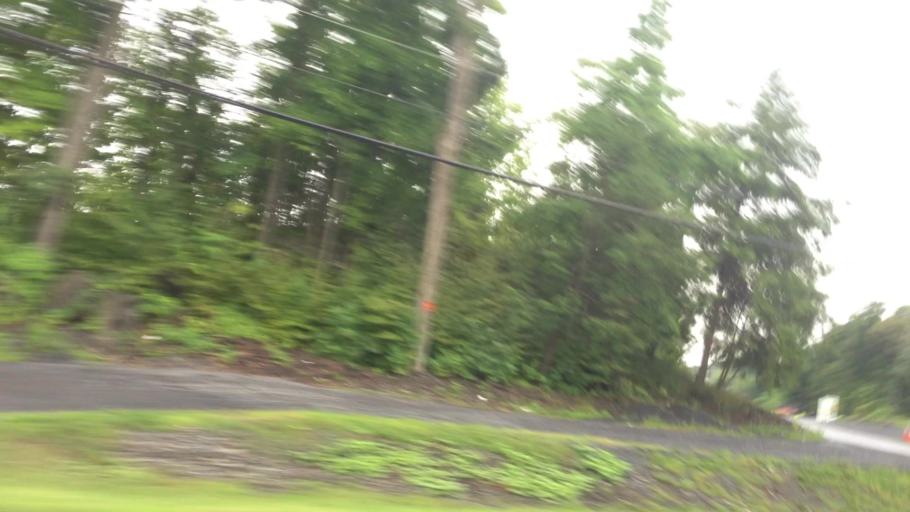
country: US
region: New York
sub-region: Ulster County
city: Lincoln Park
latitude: 41.9561
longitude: -73.9737
